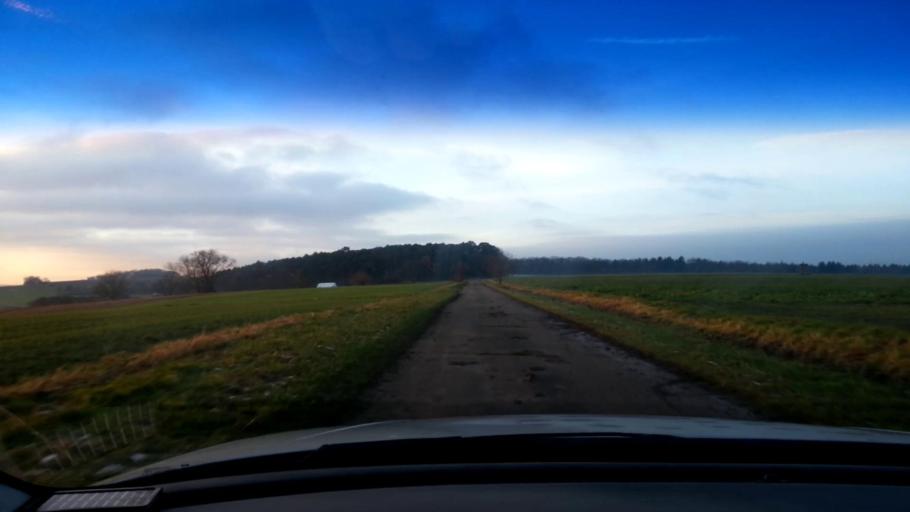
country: DE
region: Bavaria
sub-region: Upper Franconia
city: Frensdorf
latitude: 49.7902
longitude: 10.8482
